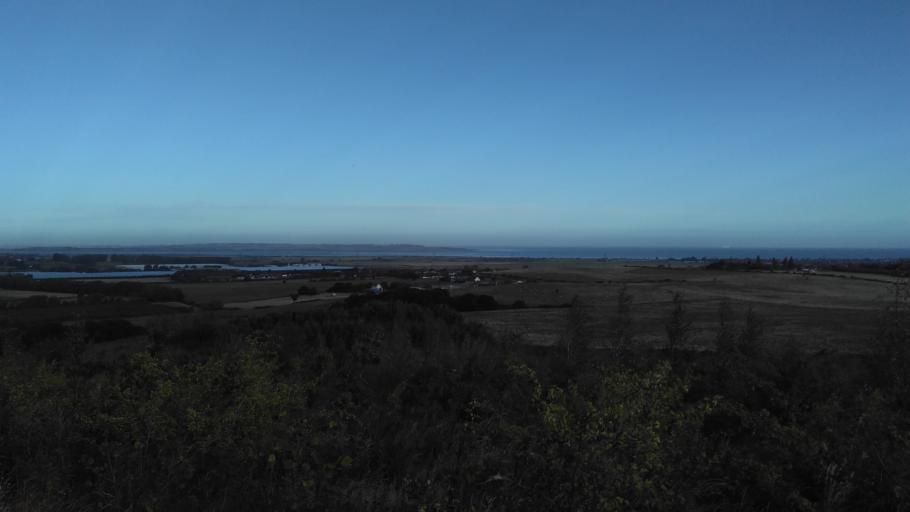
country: GB
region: England
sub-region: Kent
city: Dunkirk
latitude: 51.3139
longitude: 1.0018
